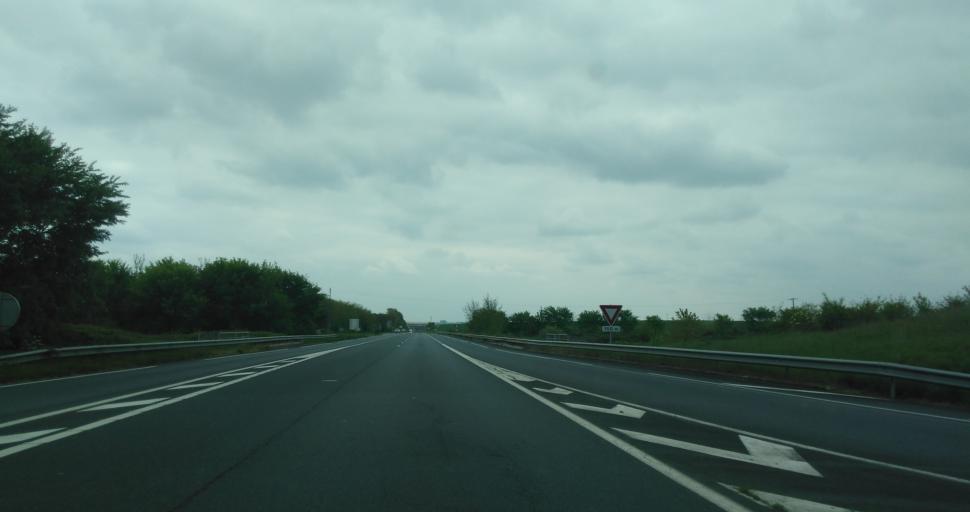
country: FR
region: Poitou-Charentes
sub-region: Departement des Deux-Sevres
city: Echire
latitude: 46.4240
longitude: -0.3972
